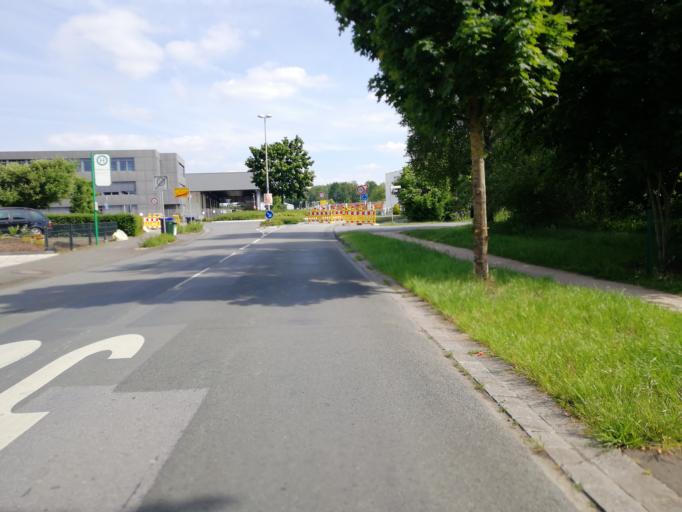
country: DE
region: North Rhine-Westphalia
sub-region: Regierungsbezirk Detmold
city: Verl
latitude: 51.8941
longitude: 8.4627
